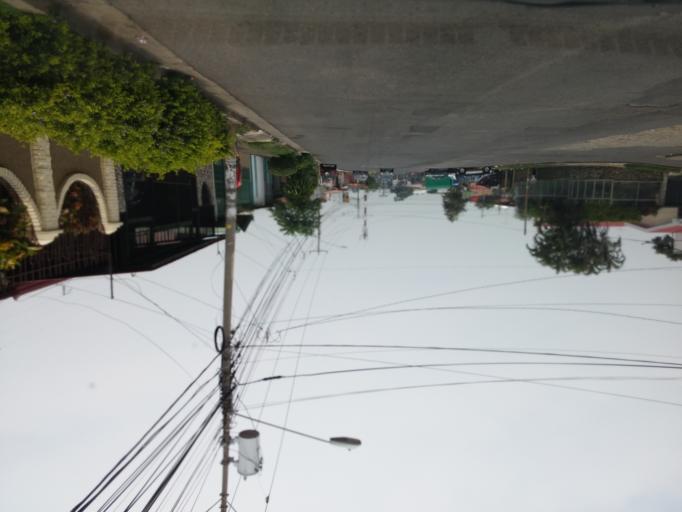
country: CR
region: Alajuela
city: Alajuela
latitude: 10.0075
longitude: -84.2045
